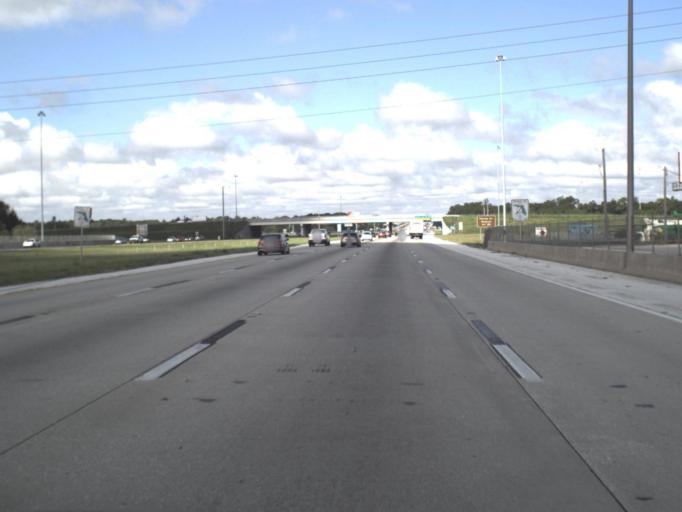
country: US
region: Florida
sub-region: Polk County
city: Winston
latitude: 28.0370
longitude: -82.0510
